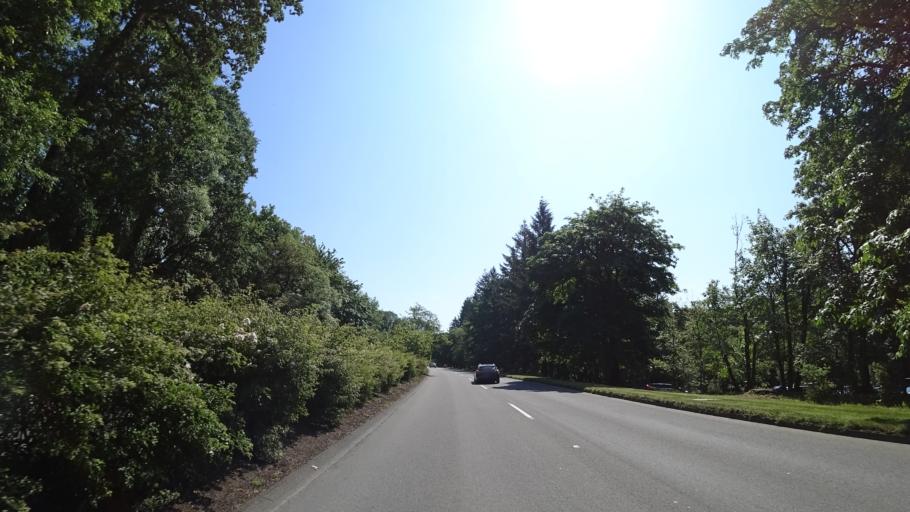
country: US
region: Oregon
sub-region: Washington County
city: Durham
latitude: 45.4190
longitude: -122.7371
